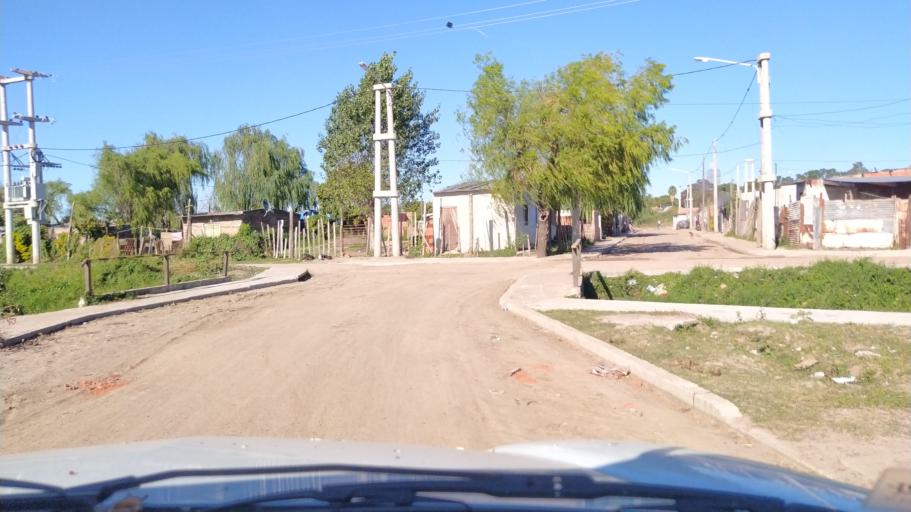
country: AR
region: Corrientes
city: Corrientes
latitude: -27.4992
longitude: -58.8036
